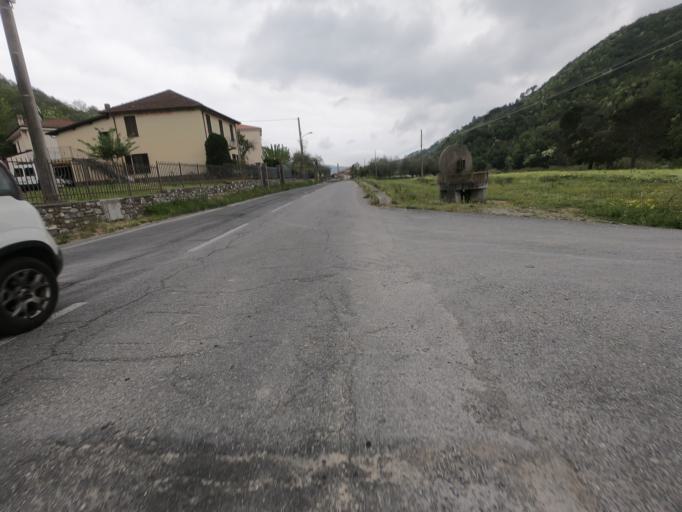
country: IT
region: Liguria
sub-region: Provincia di Savona
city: Villafranca
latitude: 44.0012
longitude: 8.1055
